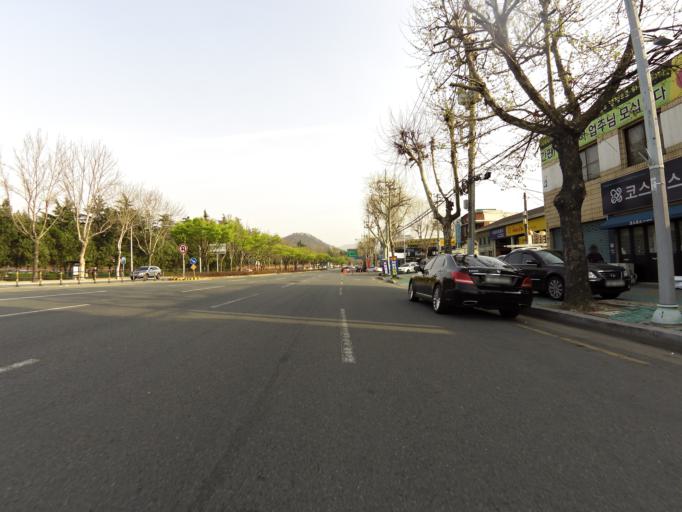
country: KR
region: Daegu
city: Daegu
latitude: 35.8725
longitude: 128.6475
